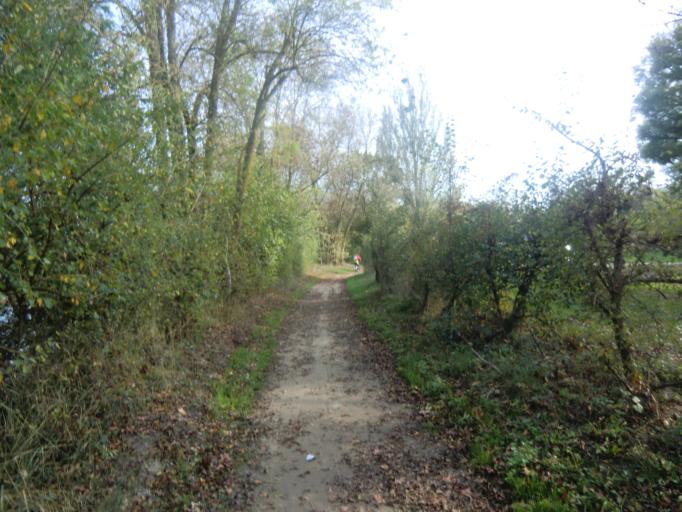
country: FR
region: Pays de la Loire
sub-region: Departement de Maine-et-Loire
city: Villebernier
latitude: 47.2420
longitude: -0.0221
